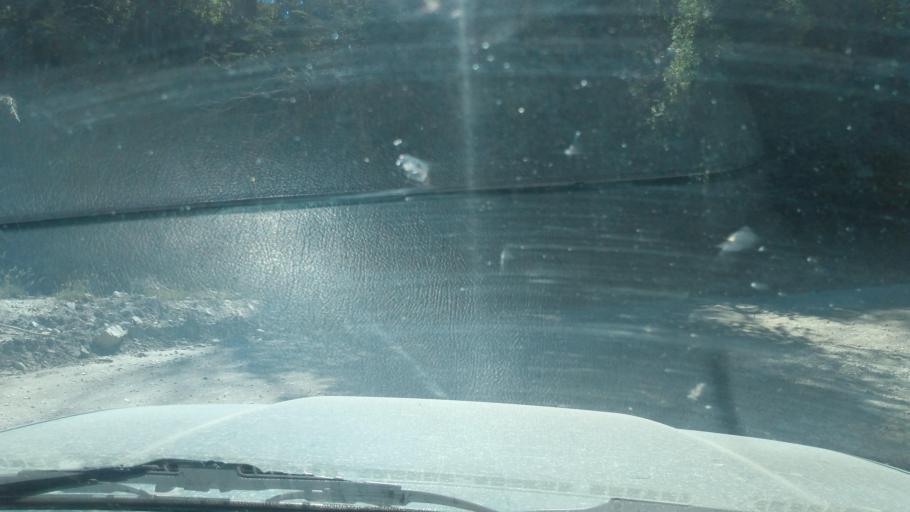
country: AR
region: Neuquen
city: Villa La Angostura
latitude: -40.6055
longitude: -71.6171
